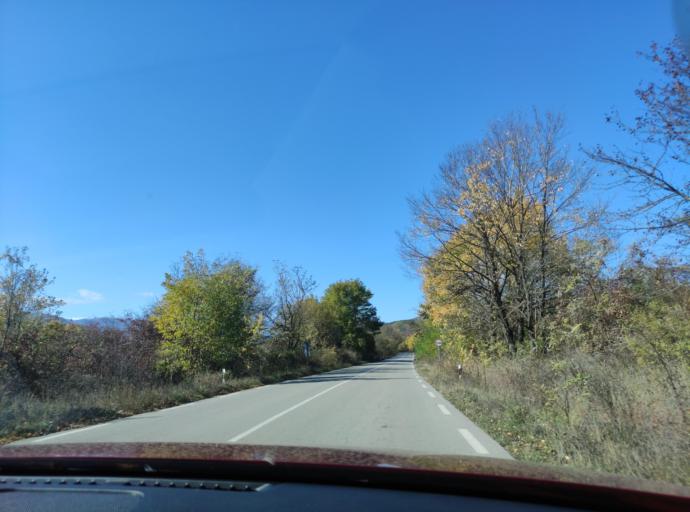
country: BG
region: Montana
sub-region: Obshtina Chiprovtsi
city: Chiprovtsi
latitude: 43.4230
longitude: 23.0154
